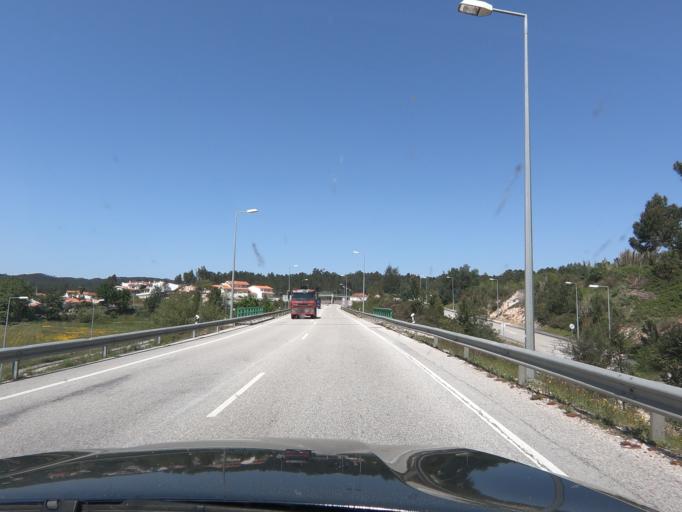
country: PT
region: Coimbra
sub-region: Miranda do Corvo
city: Miranda do Corvo
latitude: 40.0894
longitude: -8.3173
